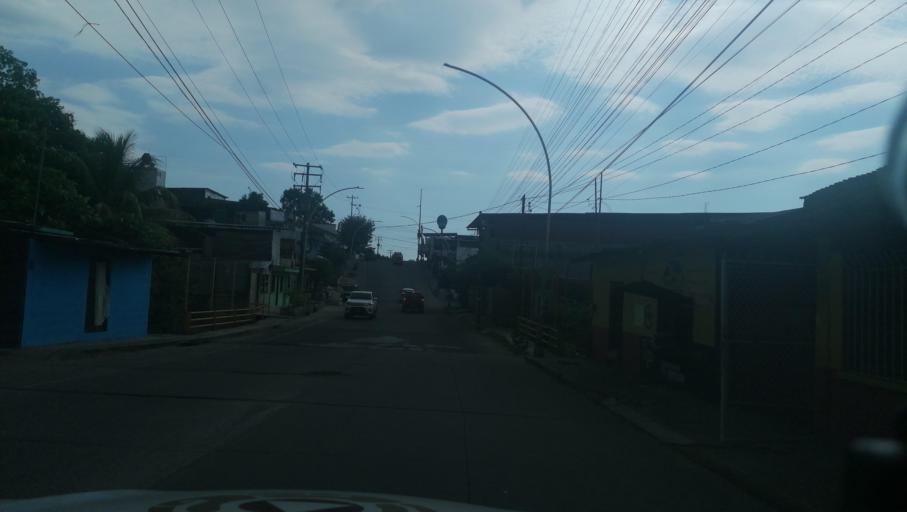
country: MX
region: Chiapas
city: Tapachula
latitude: 14.9274
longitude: -92.2530
